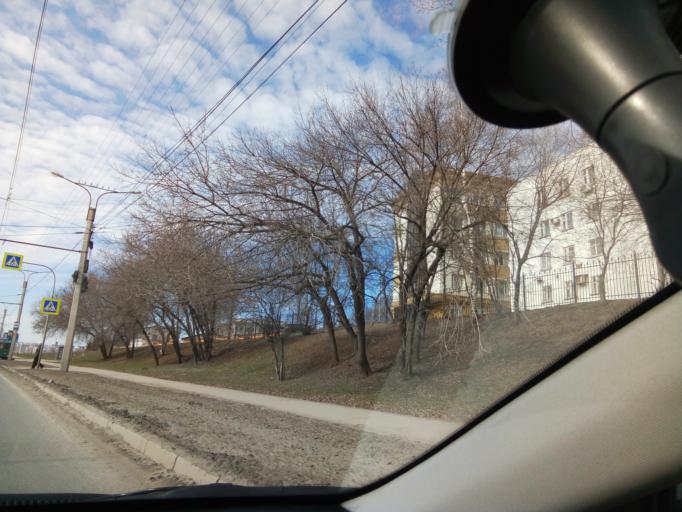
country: RU
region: Chuvashia
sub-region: Cheboksarskiy Rayon
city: Cheboksary
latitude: 56.1193
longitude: 47.2517
